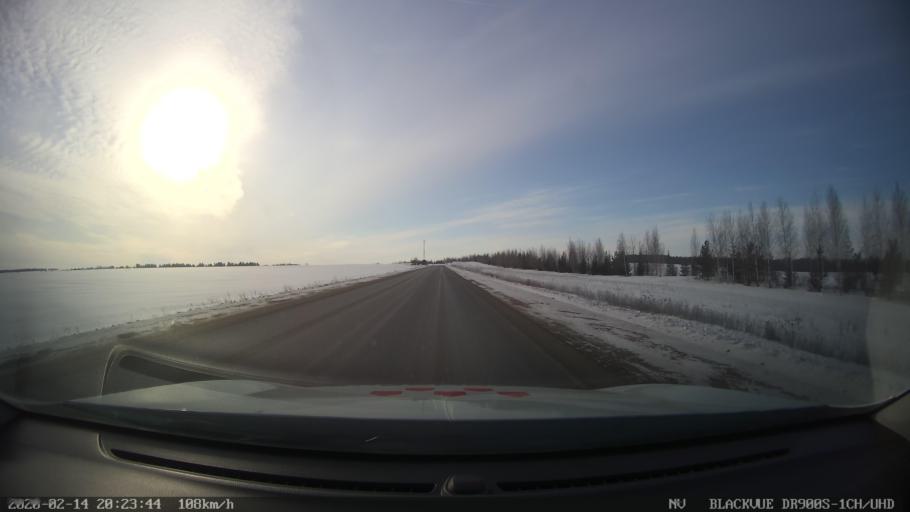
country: RU
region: Tatarstan
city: Verkhniy Uslon
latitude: 55.5237
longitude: 48.9691
